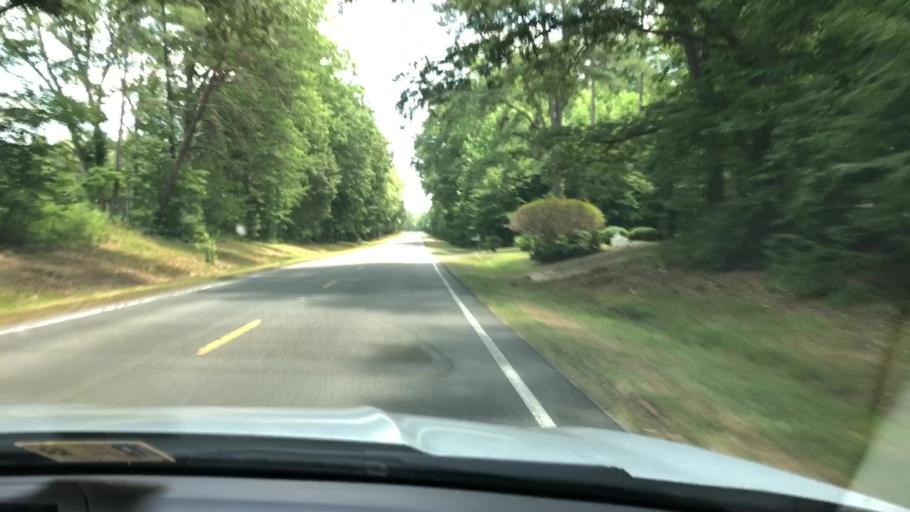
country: US
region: Virginia
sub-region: Lancaster County
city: Lancaster
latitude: 37.8077
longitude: -76.5391
